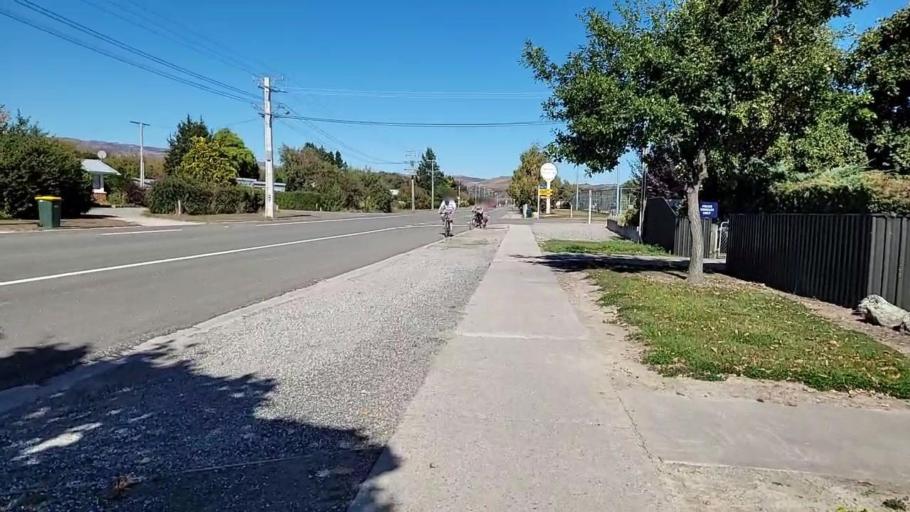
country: NZ
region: Otago
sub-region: Queenstown-Lakes District
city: Wanaka
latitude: -45.0991
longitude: 169.5973
